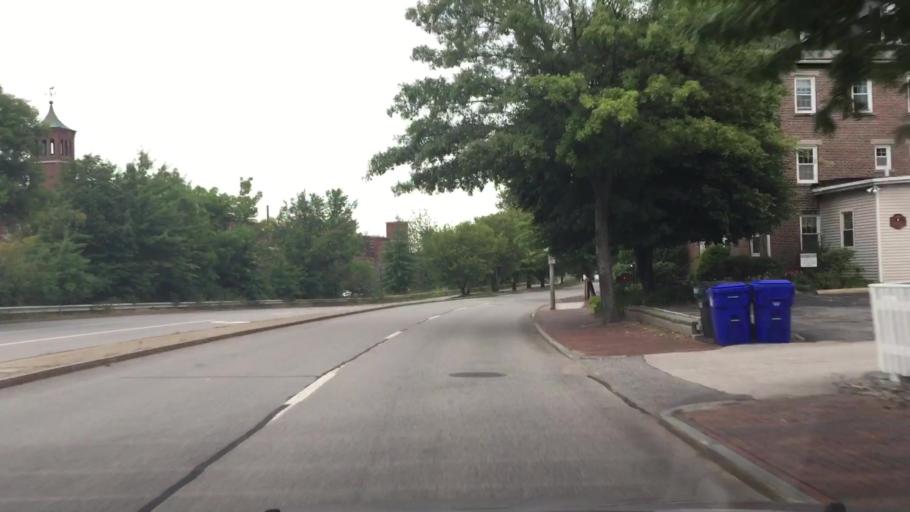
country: US
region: New Hampshire
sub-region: Hillsborough County
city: Manchester
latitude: 42.9896
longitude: -71.4669
